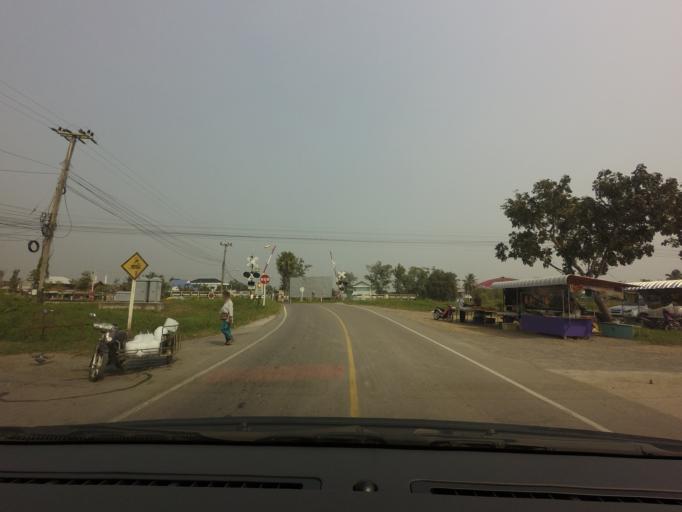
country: TH
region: Prachuap Khiri Khan
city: Kui Buri
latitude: 12.0678
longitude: 99.8720
